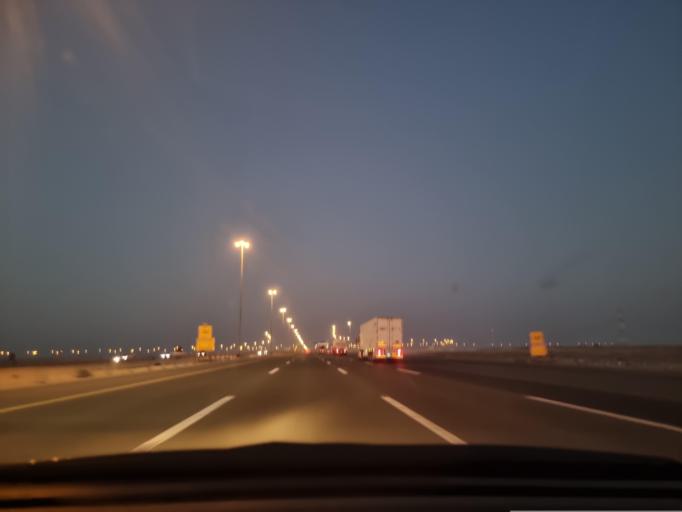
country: AE
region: Abu Dhabi
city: Abu Dhabi
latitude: 24.6629
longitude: 54.8047
